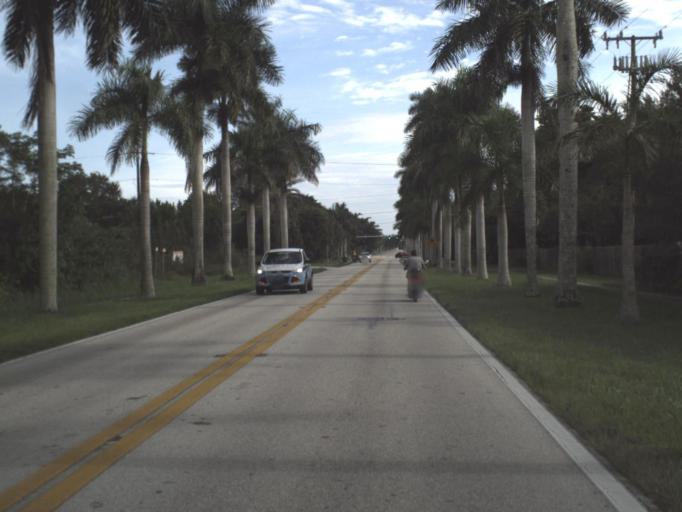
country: US
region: Florida
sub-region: Lee County
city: Whiskey Creek
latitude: 26.5727
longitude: -81.9007
